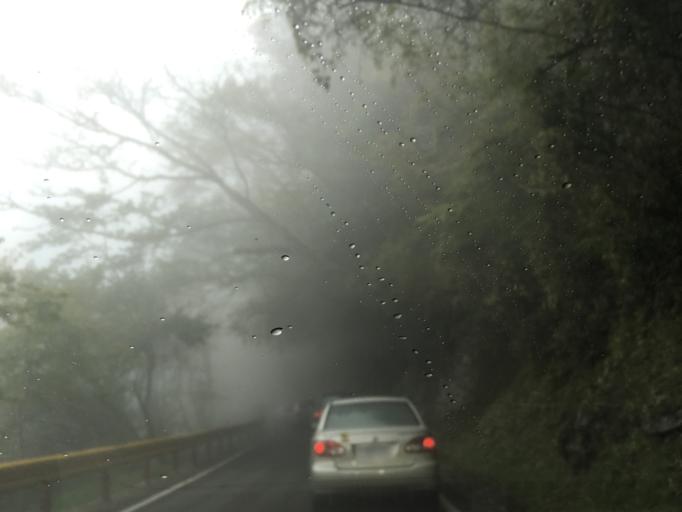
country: TW
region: Taiwan
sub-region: Hualien
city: Hualian
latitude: 24.1849
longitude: 121.4215
